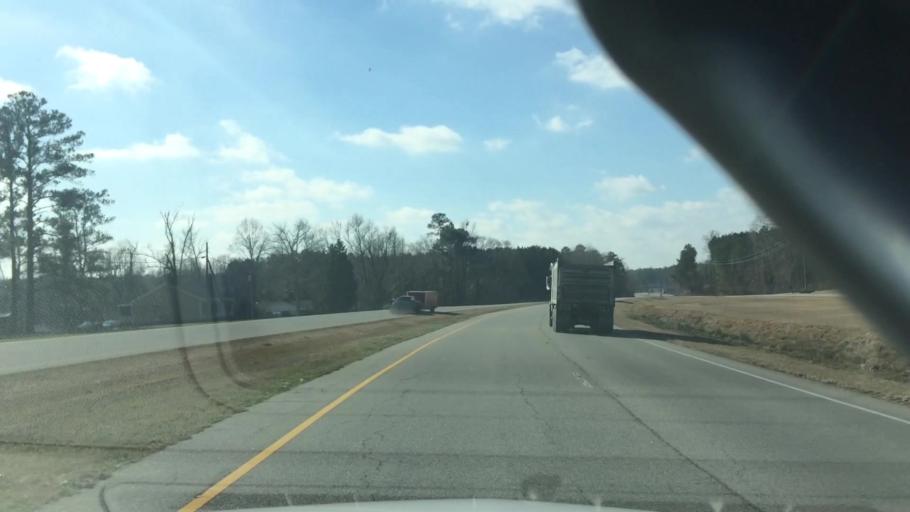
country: US
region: North Carolina
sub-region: Lenoir County
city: Kinston
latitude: 35.3120
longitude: -77.5178
